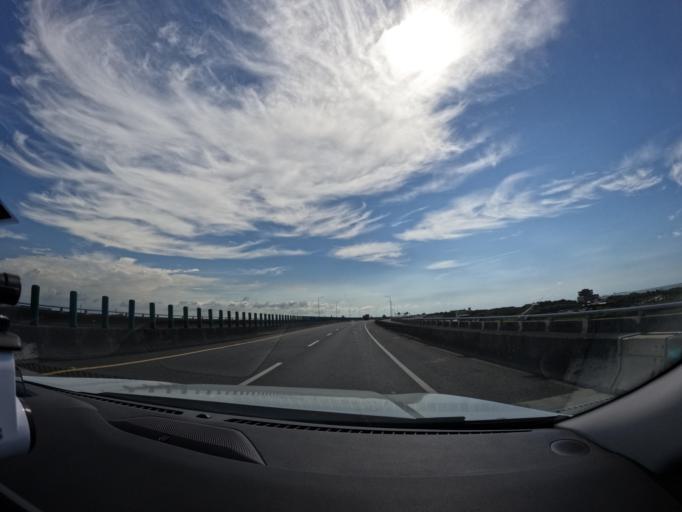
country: TW
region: Taiwan
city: Taoyuan City
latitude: 25.1132
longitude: 121.2459
